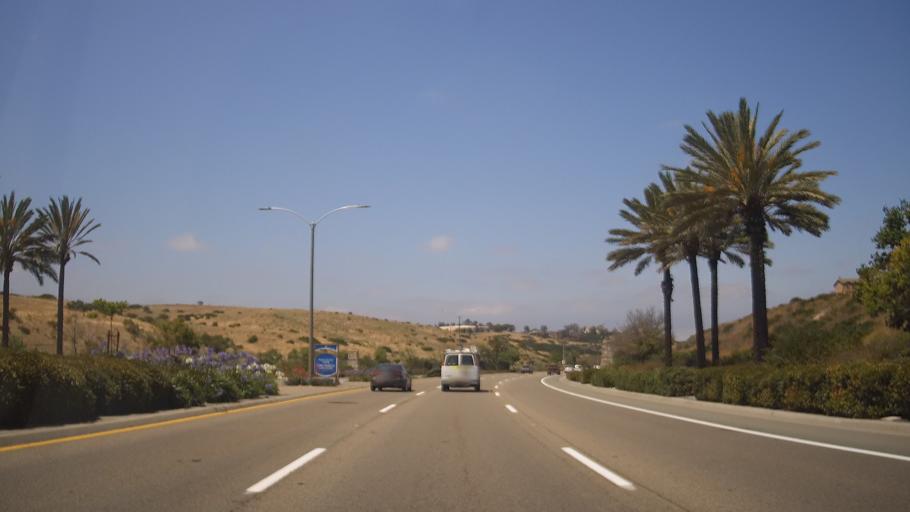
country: US
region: California
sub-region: San Diego County
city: Bonita
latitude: 32.6118
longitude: -117.0116
